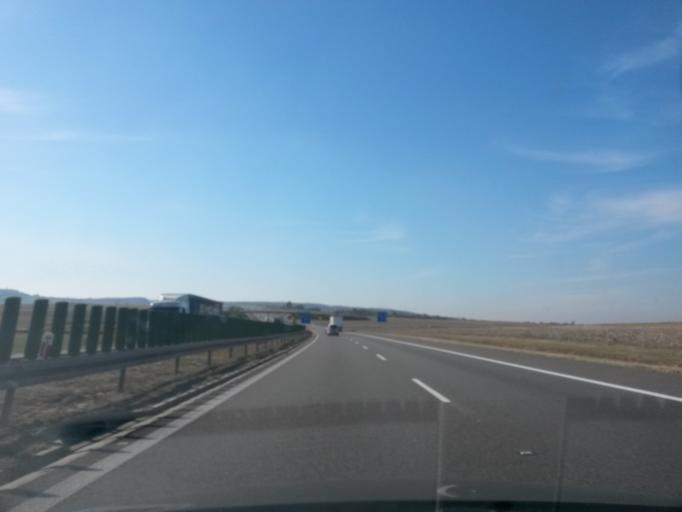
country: PL
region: Opole Voivodeship
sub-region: Powiat strzelecki
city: Lesnica
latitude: 50.4657
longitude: 18.2151
